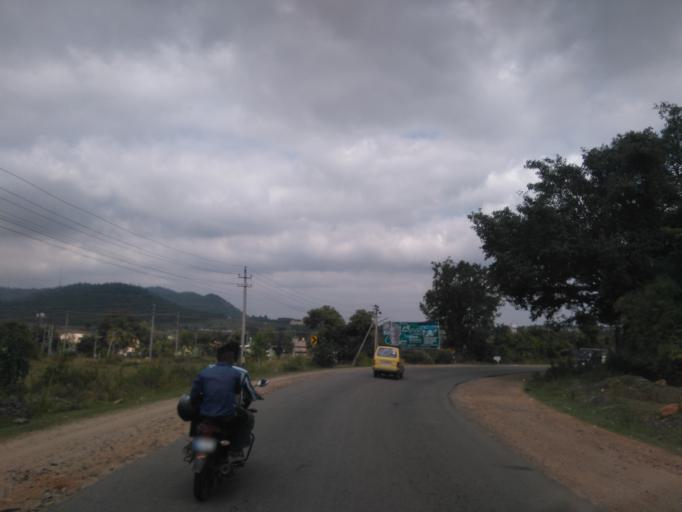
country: IN
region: Karnataka
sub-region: Mysore
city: Mysore
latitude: 12.2899
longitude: 76.7105
